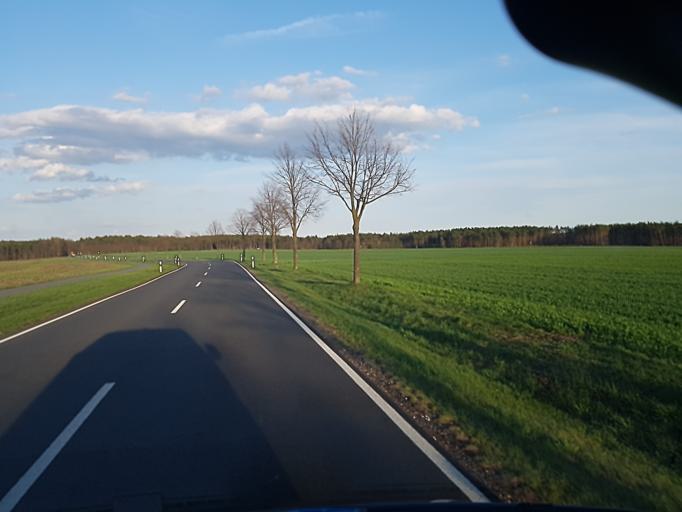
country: DE
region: Saxony
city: Kossa
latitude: 51.5771
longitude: 12.7164
